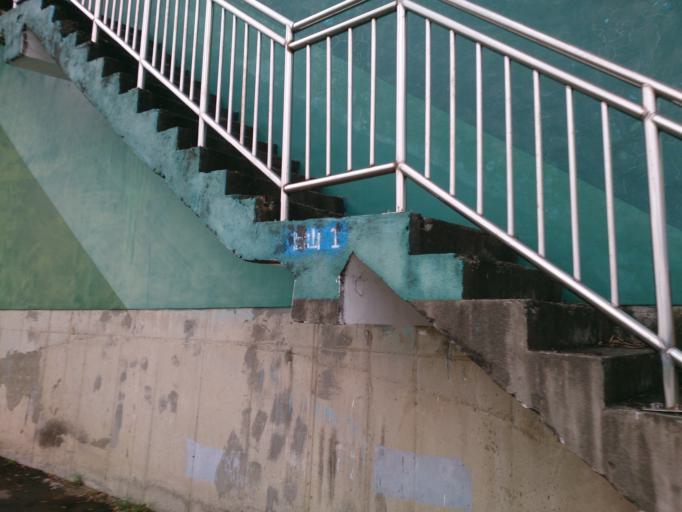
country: TW
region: Taipei
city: Taipei
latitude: 25.0775
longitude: 121.5394
